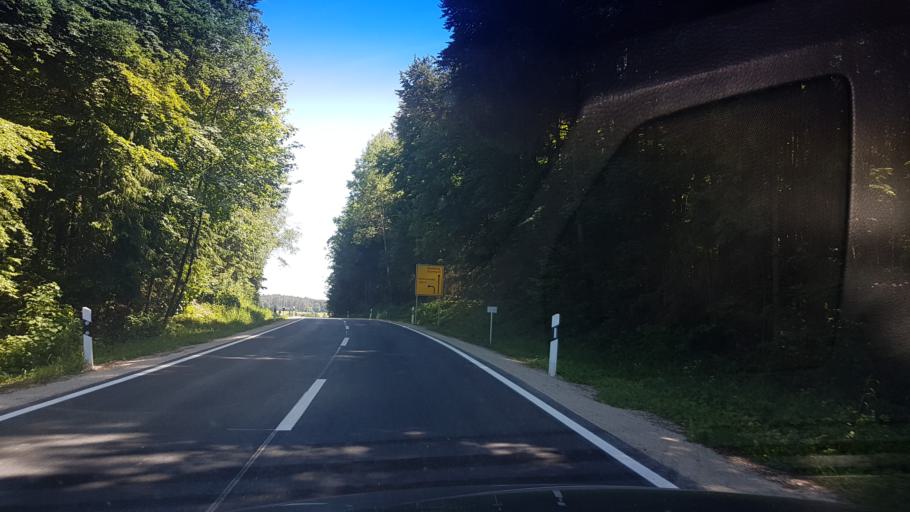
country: DE
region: Bavaria
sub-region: Upper Franconia
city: Weismain
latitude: 50.0370
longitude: 11.2594
